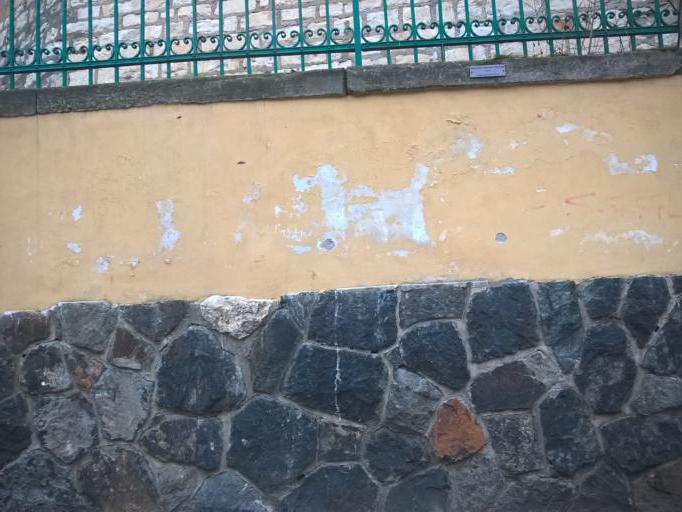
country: CZ
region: Praha
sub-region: Praha 1
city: Mala Strana
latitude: 50.0762
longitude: 14.3987
